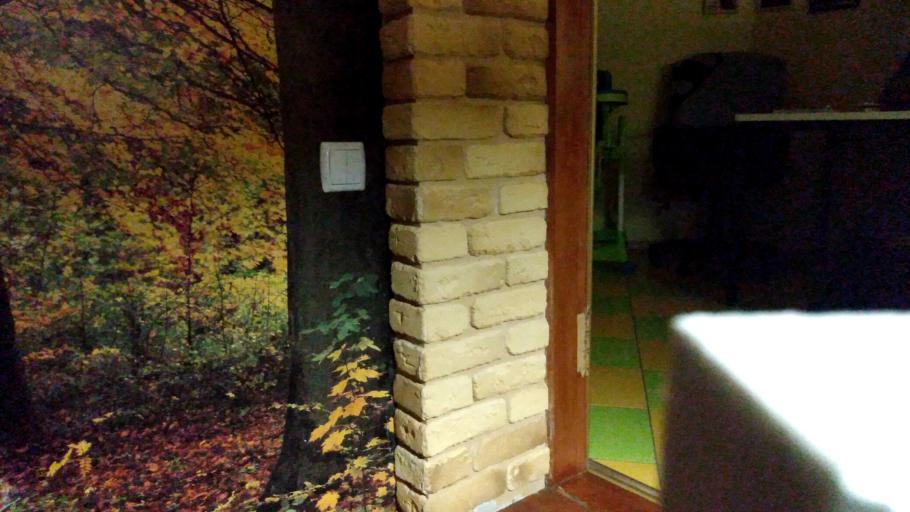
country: RU
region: Vologda
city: Lipin Bor
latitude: 60.8174
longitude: 38.0268
